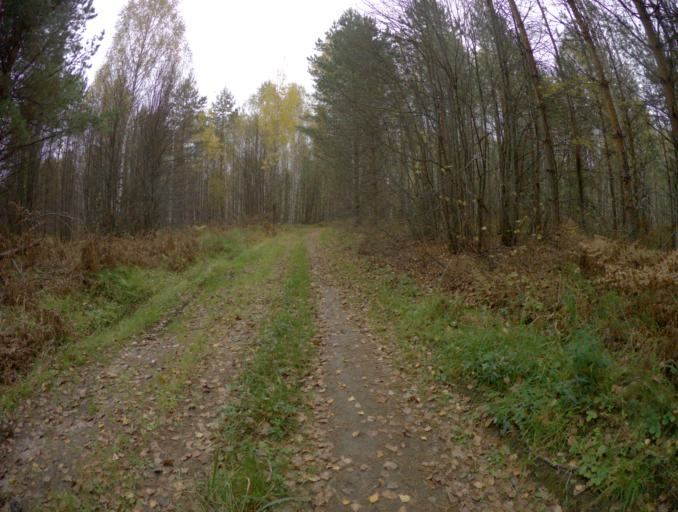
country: RU
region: Vladimir
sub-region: Kovrovskiy Rayon
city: Kovrov
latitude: 56.3122
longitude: 41.5228
